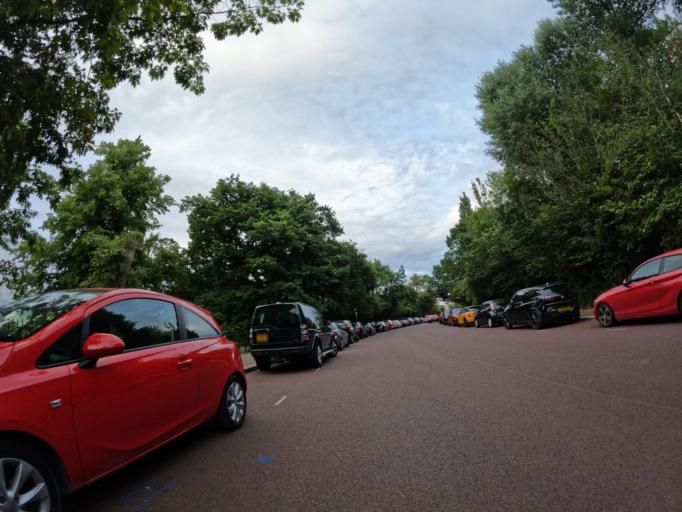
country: GB
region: England
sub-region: Greater London
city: Camden Town
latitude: 51.5290
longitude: -0.1543
